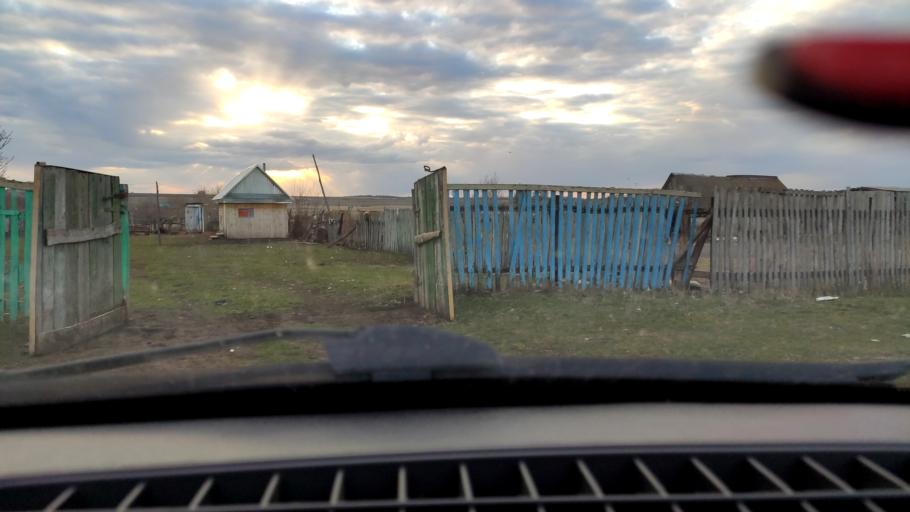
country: RU
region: Bashkortostan
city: Tolbazy
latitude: 54.0180
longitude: 55.5321
